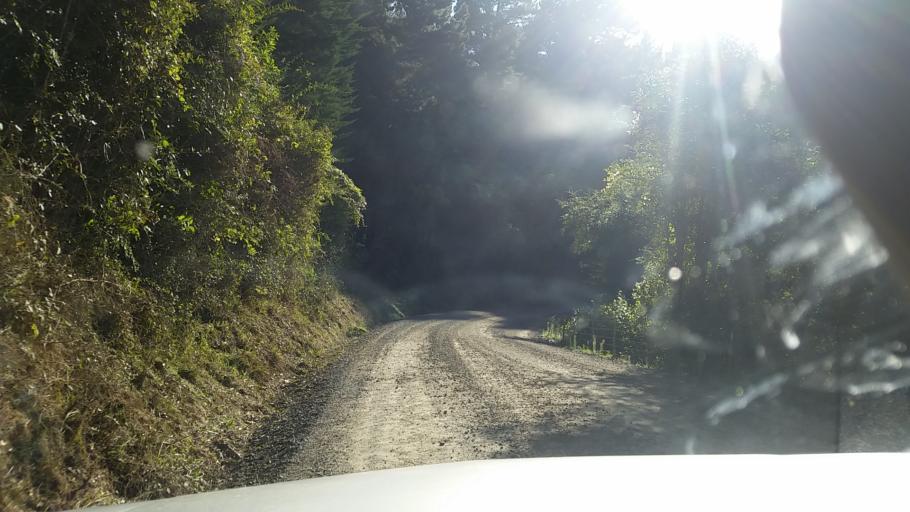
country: NZ
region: Marlborough
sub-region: Marlborough District
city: Blenheim
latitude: -41.4457
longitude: 173.8830
